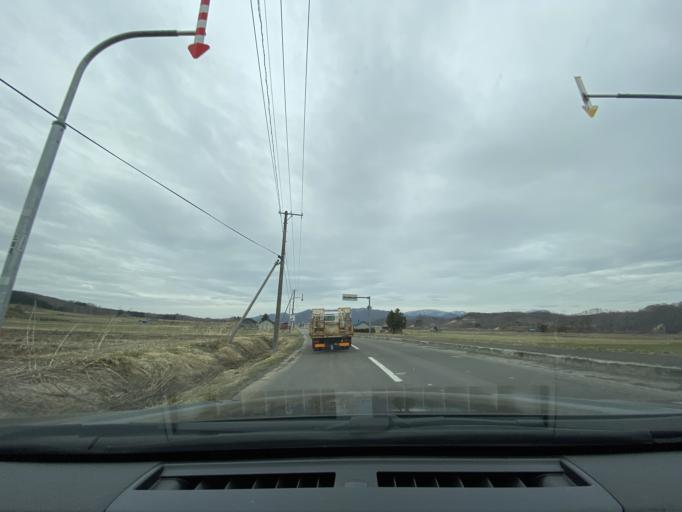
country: JP
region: Hokkaido
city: Nayoro
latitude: 44.0930
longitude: 142.4732
